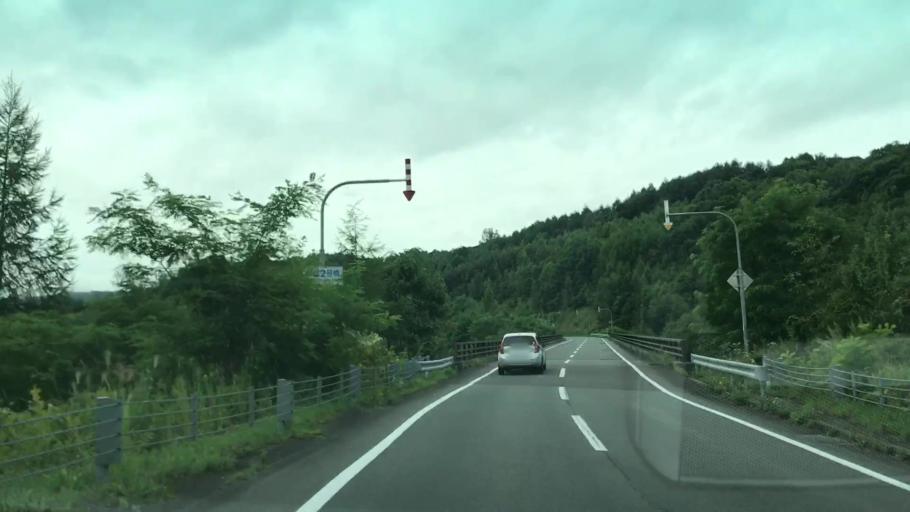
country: JP
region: Hokkaido
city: Yoichi
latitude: 43.1487
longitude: 140.8219
